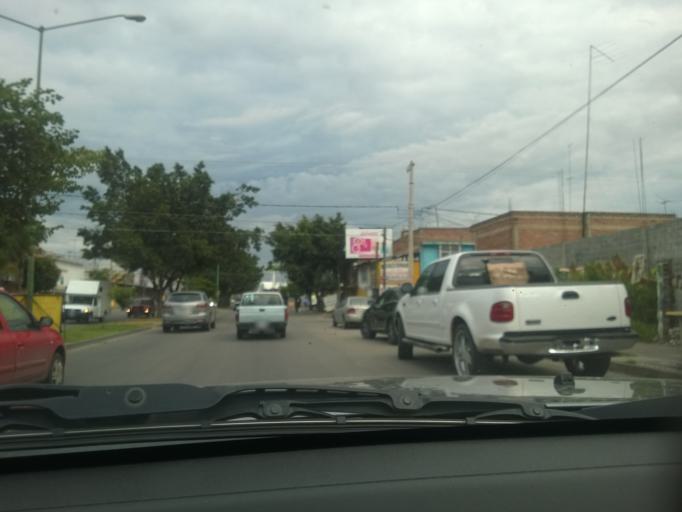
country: MX
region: Guanajuato
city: Leon
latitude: 21.1330
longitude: -101.6725
